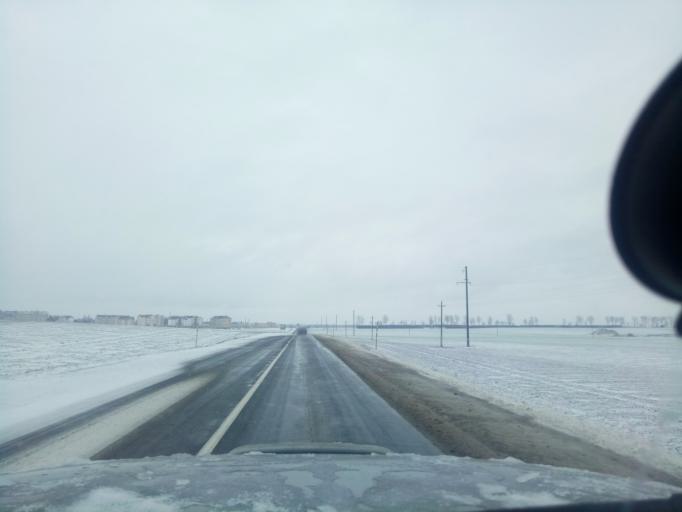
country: BY
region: Minsk
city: Nyasvizh
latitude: 53.2371
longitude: 26.6347
